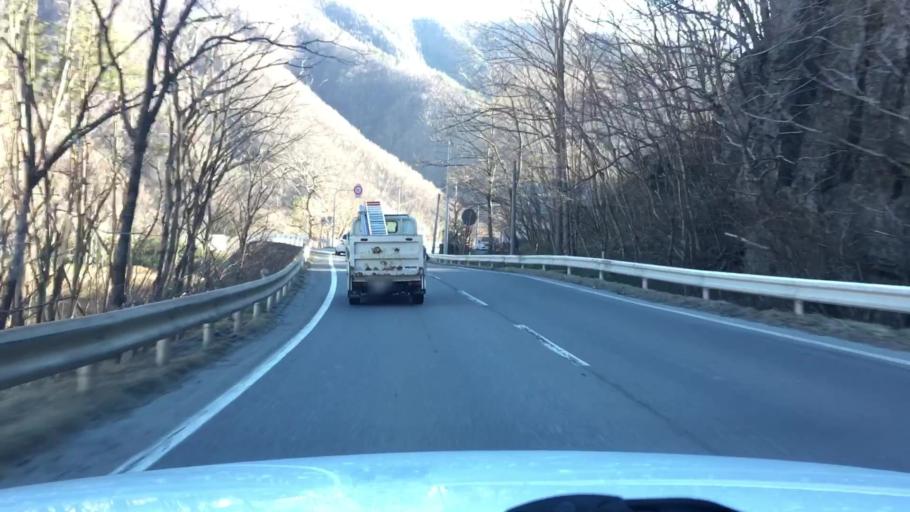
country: JP
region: Iwate
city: Miyako
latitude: 39.6241
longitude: 141.8097
